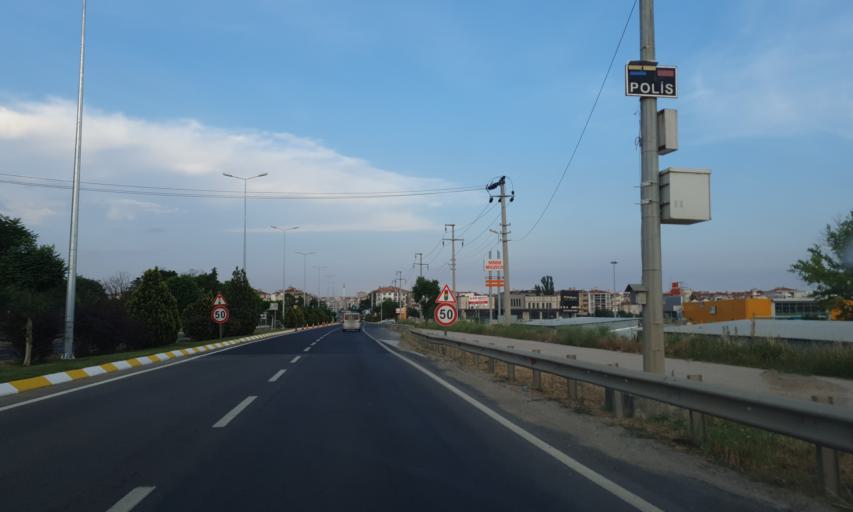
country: TR
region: Kirklareli
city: Luleburgaz
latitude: 41.4044
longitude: 27.3426
